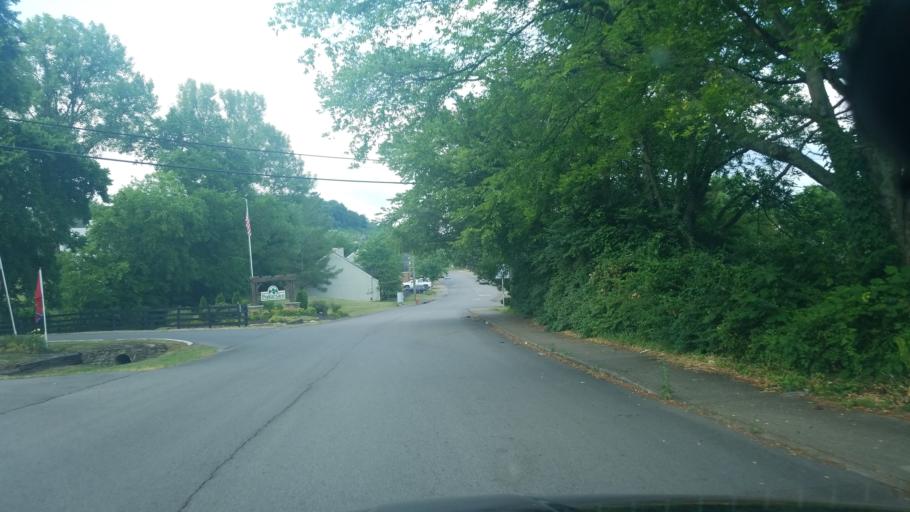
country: US
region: Tennessee
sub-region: Davidson County
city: Nashville
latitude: 36.2284
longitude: -86.7441
